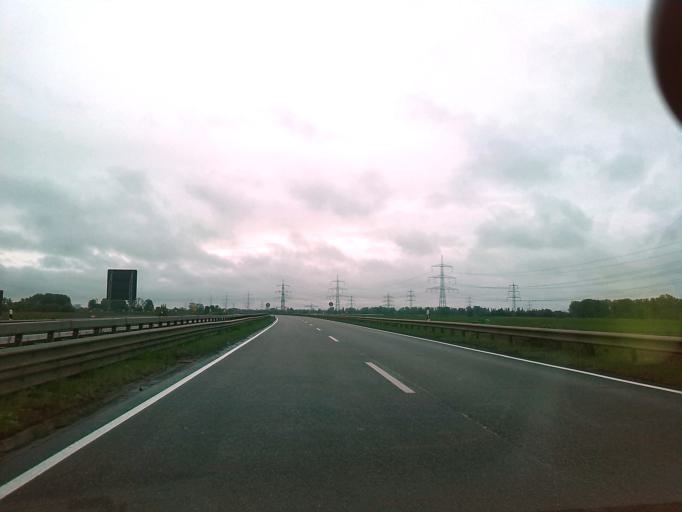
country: DE
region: Rheinland-Pfalz
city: Bobenheim-Roxheim
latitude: 49.5784
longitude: 8.4013
